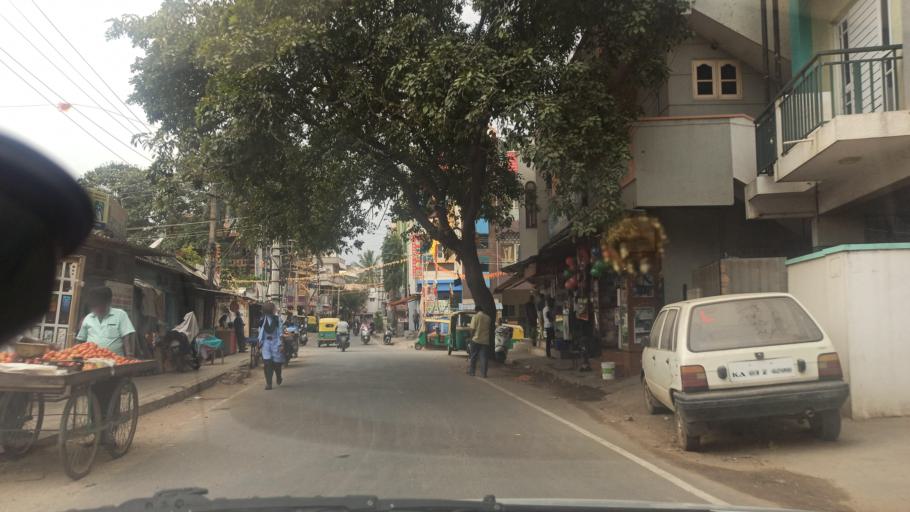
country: IN
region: Karnataka
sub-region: Bangalore Urban
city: Bangalore
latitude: 13.0353
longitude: 77.6019
